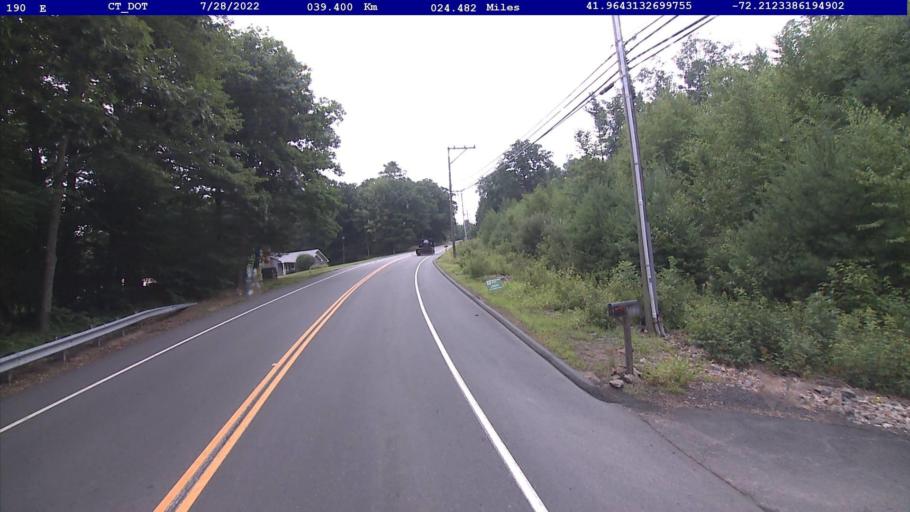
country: US
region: Connecticut
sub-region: Tolland County
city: Stafford
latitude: 41.9642
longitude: -72.2123
